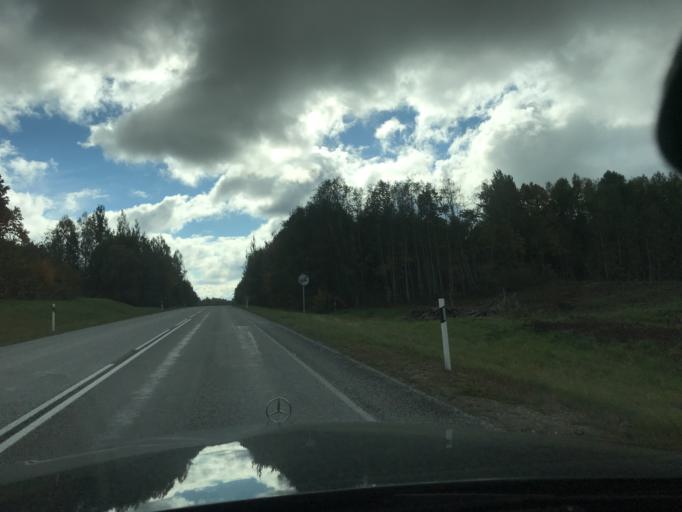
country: RU
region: Pskov
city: Pechory
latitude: 57.7007
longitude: 27.3252
